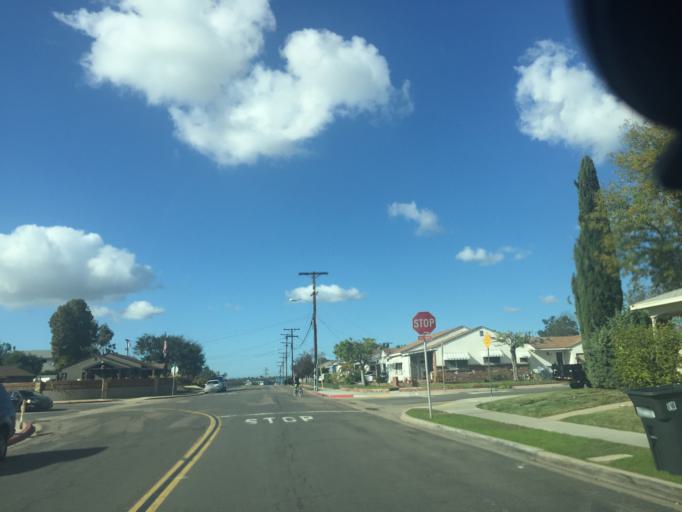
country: US
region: California
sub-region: San Diego County
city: La Mesa
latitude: 32.7913
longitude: -117.0852
